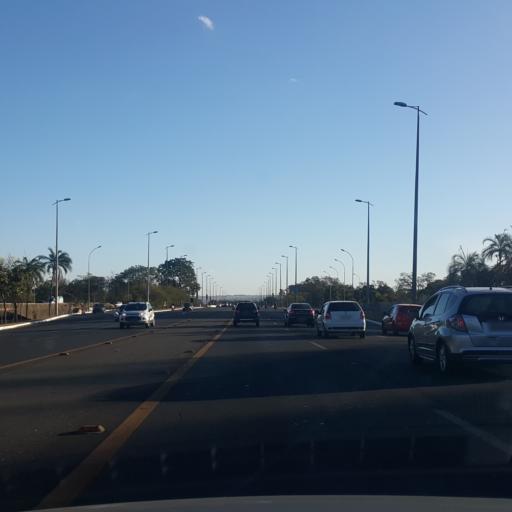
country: BR
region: Federal District
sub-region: Brasilia
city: Brasilia
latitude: -15.8335
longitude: -47.9236
